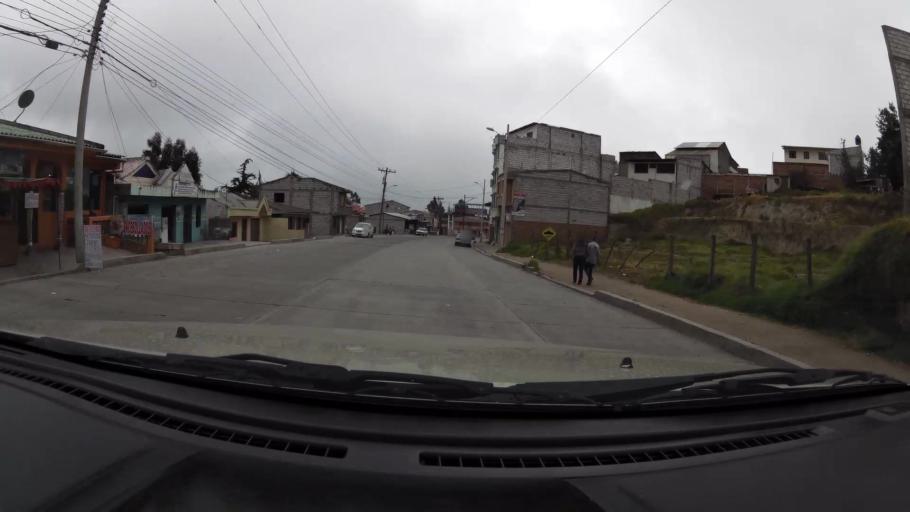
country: EC
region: Canar
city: Canar
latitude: -2.5578
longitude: -78.9405
